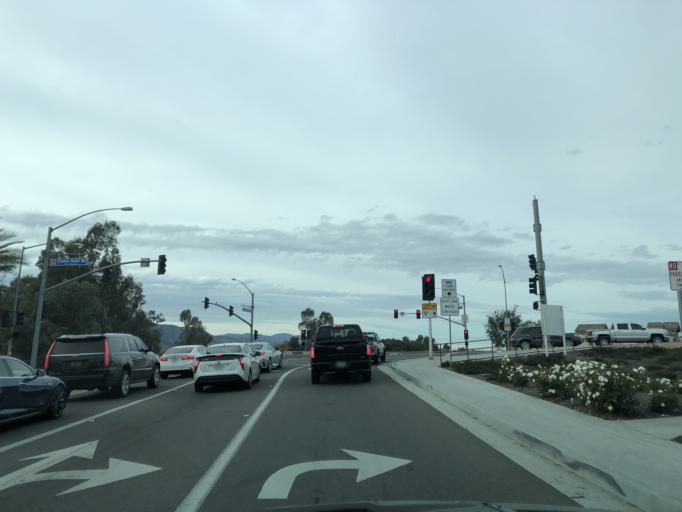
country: US
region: California
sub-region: Riverside County
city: Wildomar
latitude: 33.5940
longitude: -117.2465
